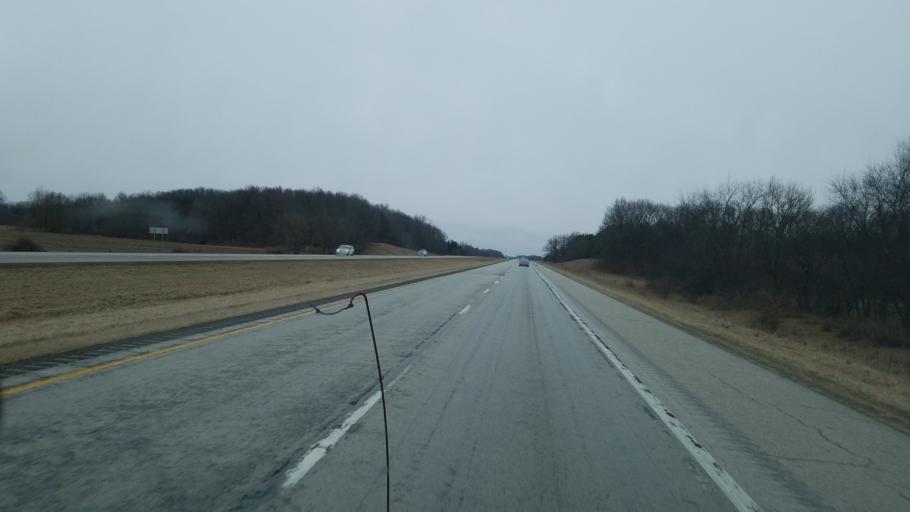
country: US
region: Indiana
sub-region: Fulton County
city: Rochester
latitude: 41.0739
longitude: -86.2401
